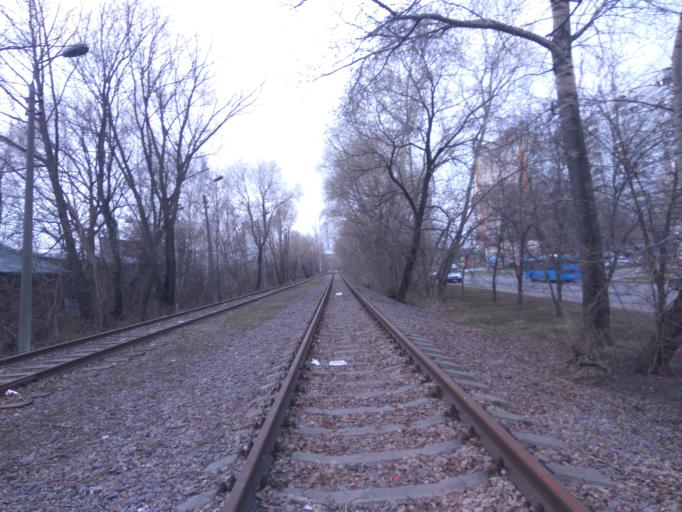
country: RU
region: Moscow
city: Vagonoremont
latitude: 55.9012
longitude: 37.5521
